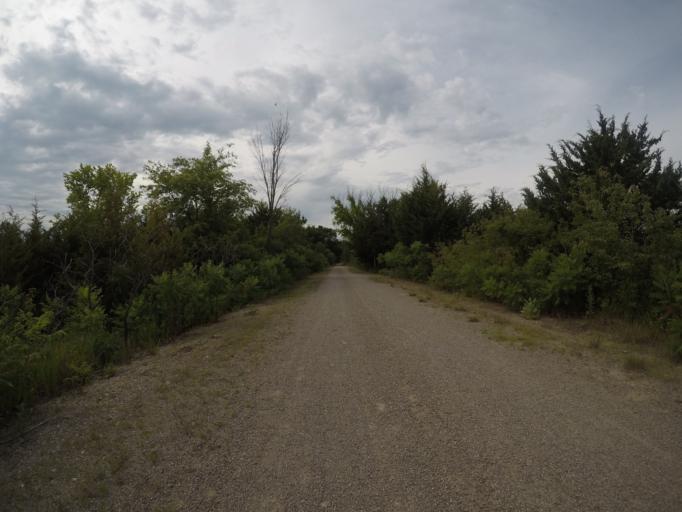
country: US
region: Kansas
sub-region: Anderson County
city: Garnett
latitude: 38.4408
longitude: -95.2643
